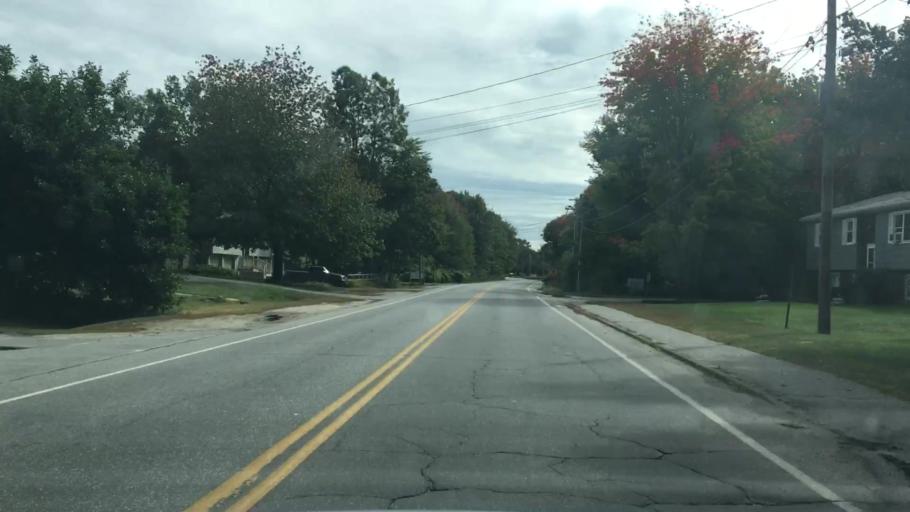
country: US
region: Maine
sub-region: Cumberland County
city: Brunswick
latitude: 43.9024
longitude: -69.9797
